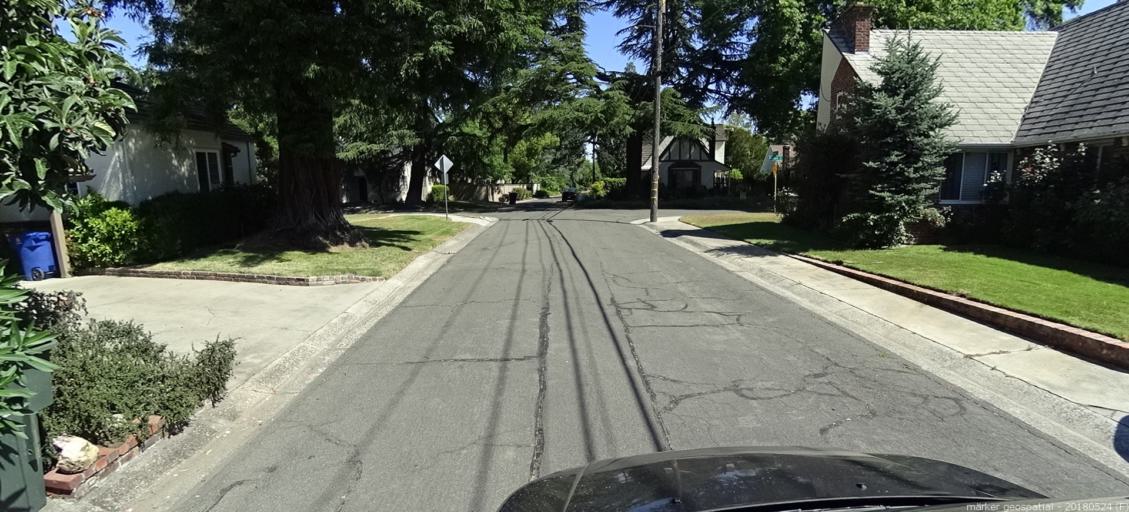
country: US
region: California
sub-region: Sacramento County
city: Sacramento
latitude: 38.6017
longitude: -121.4541
